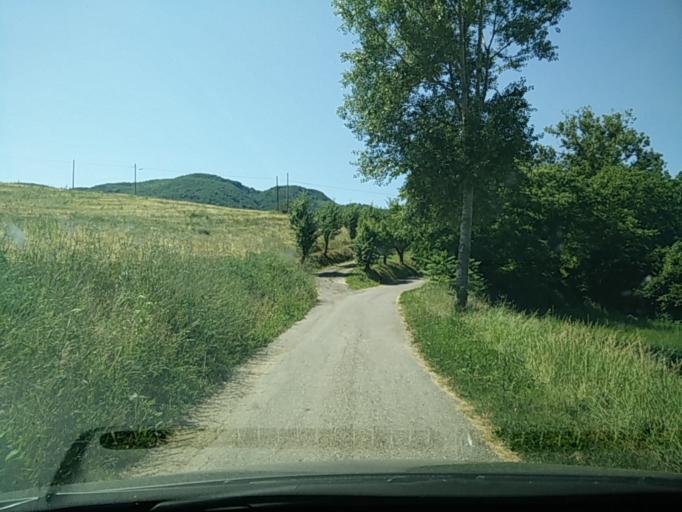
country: IT
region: Lombardy
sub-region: Provincia di Pavia
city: Susella
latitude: 44.8991
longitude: 9.1044
